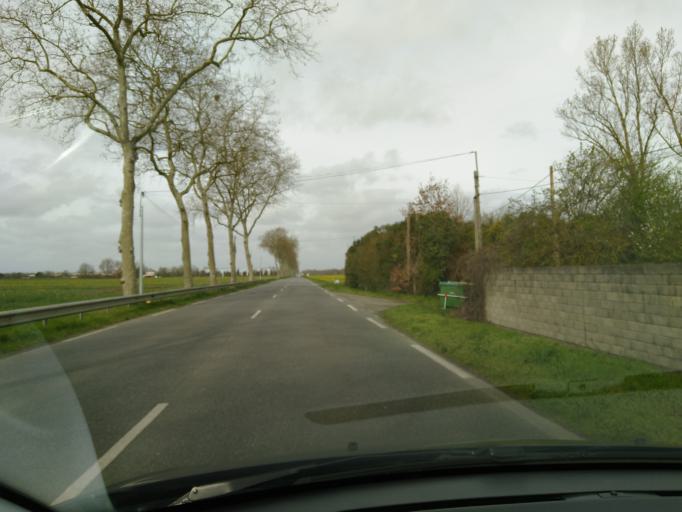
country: FR
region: Midi-Pyrenees
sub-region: Departement de la Haute-Garonne
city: Seilh
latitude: 43.7118
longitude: 1.3380
